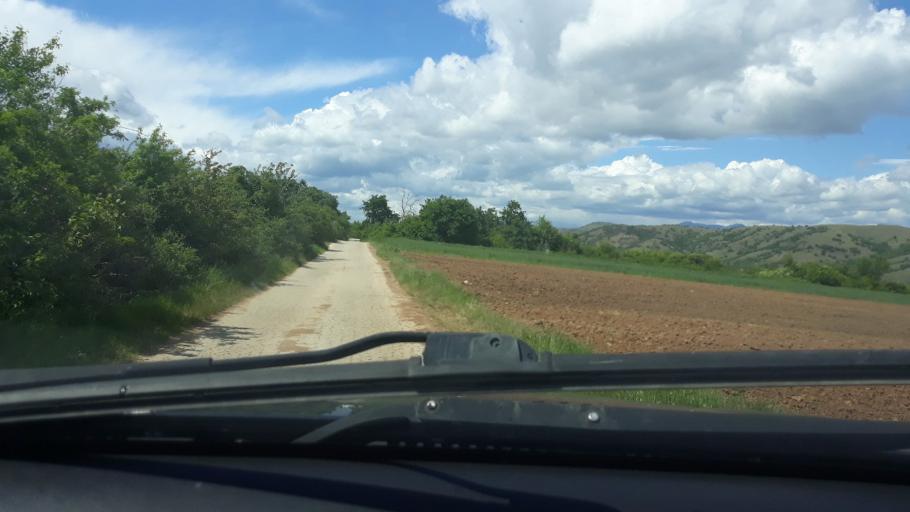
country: MK
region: Krivogastani
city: Krivogashtani
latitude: 41.3322
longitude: 21.3023
